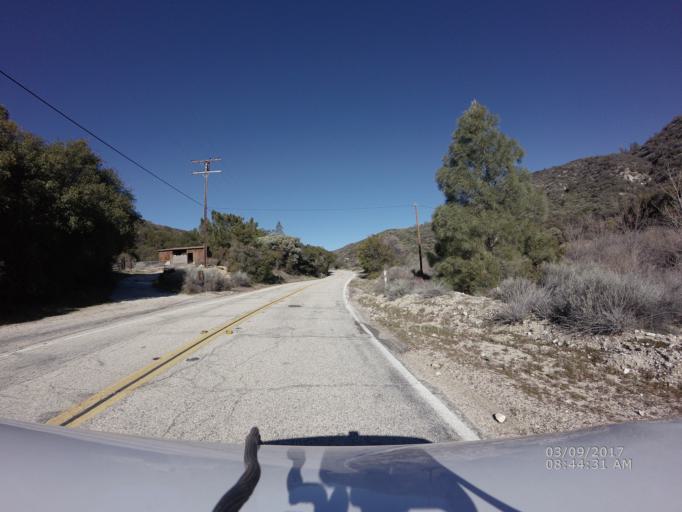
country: US
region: California
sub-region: Los Angeles County
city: Green Valley
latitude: 34.6952
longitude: -118.4983
